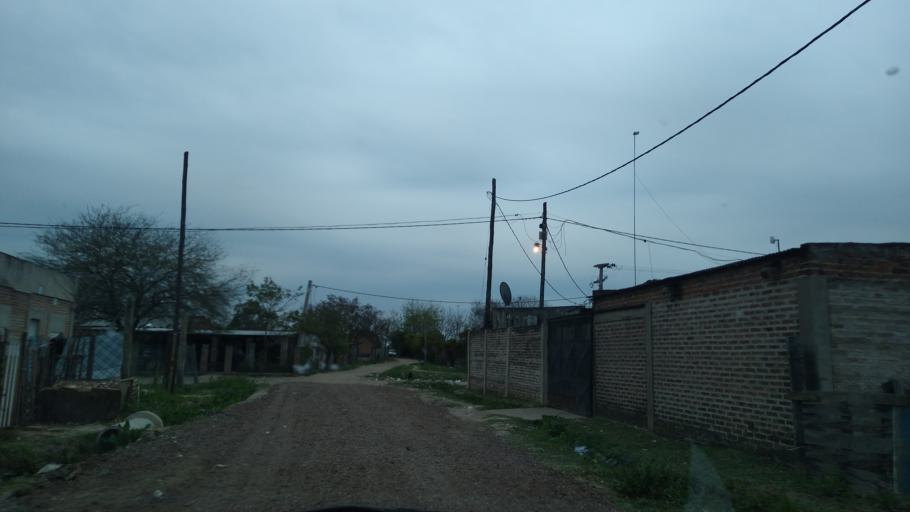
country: AR
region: Chaco
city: Resistencia
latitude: -27.4621
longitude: -58.9592
